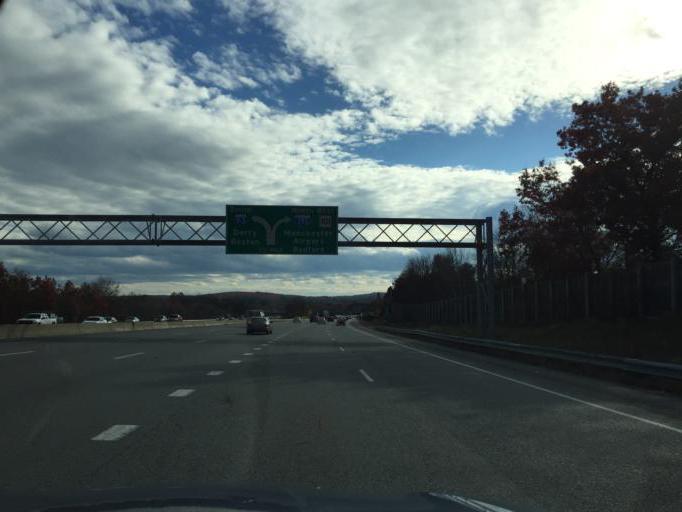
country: US
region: New Hampshire
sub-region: Hillsborough County
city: Manchester
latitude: 42.9766
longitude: -71.4144
